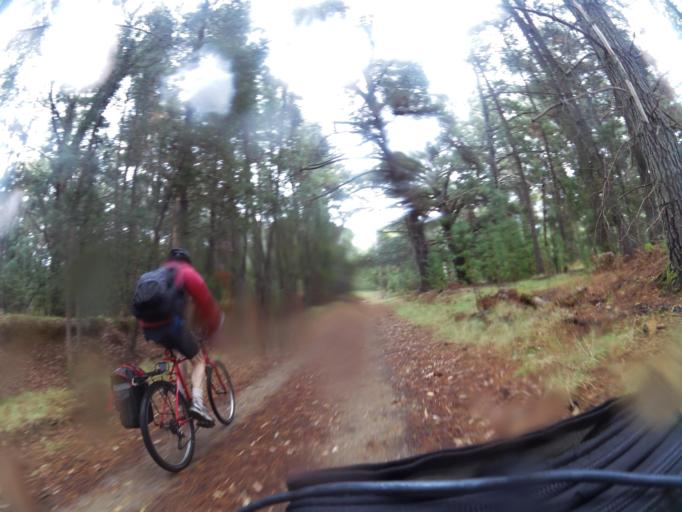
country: AU
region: New South Wales
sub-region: Greater Hume Shire
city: Holbrook
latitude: -36.1890
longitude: 147.5441
